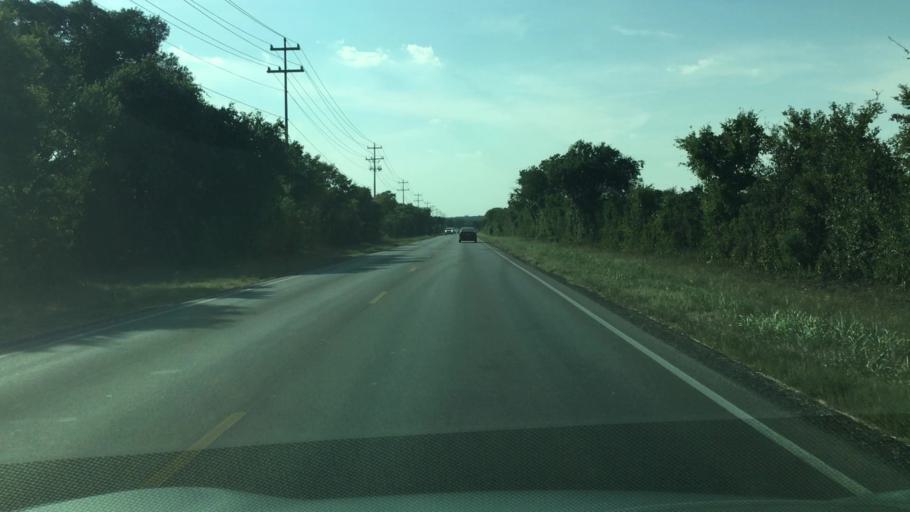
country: US
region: Texas
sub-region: Travis County
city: Shady Hollow
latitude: 30.1084
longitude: -97.9452
